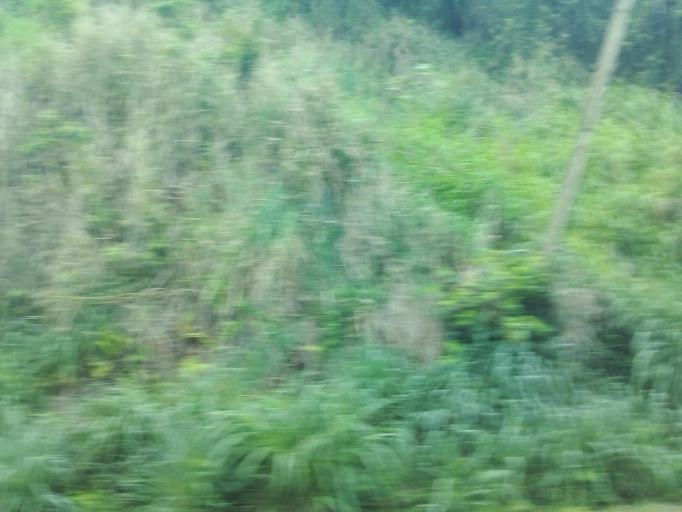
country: BR
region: Minas Gerais
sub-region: Joao Monlevade
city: Joao Monlevade
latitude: -19.8315
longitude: -43.1279
